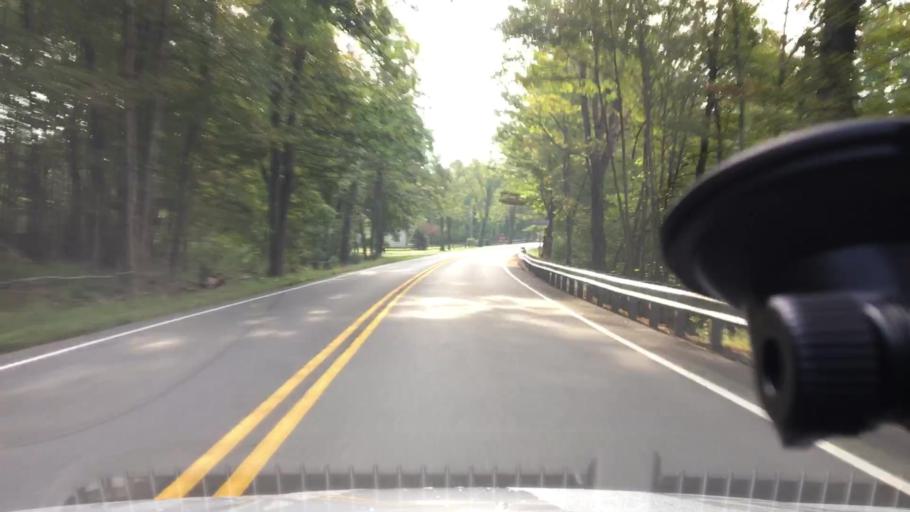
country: US
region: Pennsylvania
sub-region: Monroe County
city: Parkside
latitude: 41.1247
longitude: -75.2869
